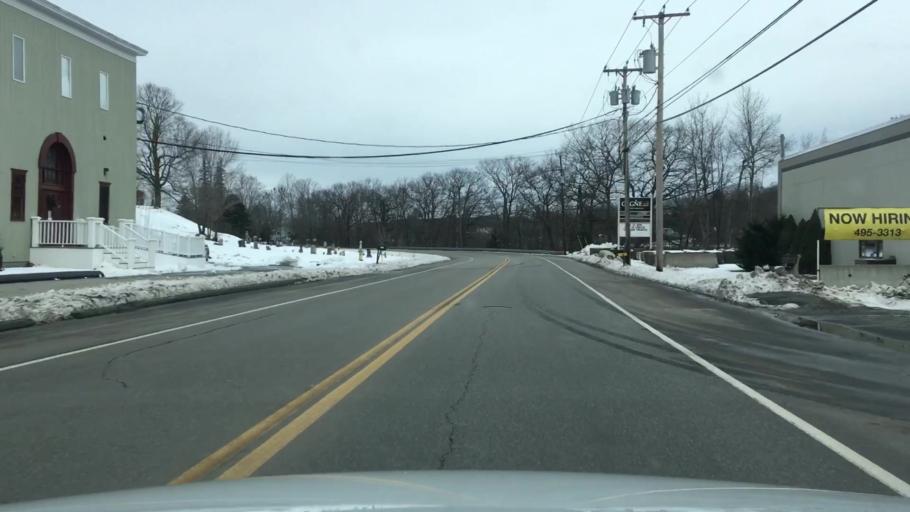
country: US
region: Maine
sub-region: Androscoggin County
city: Lewiston
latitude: 44.0793
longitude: -70.2108
